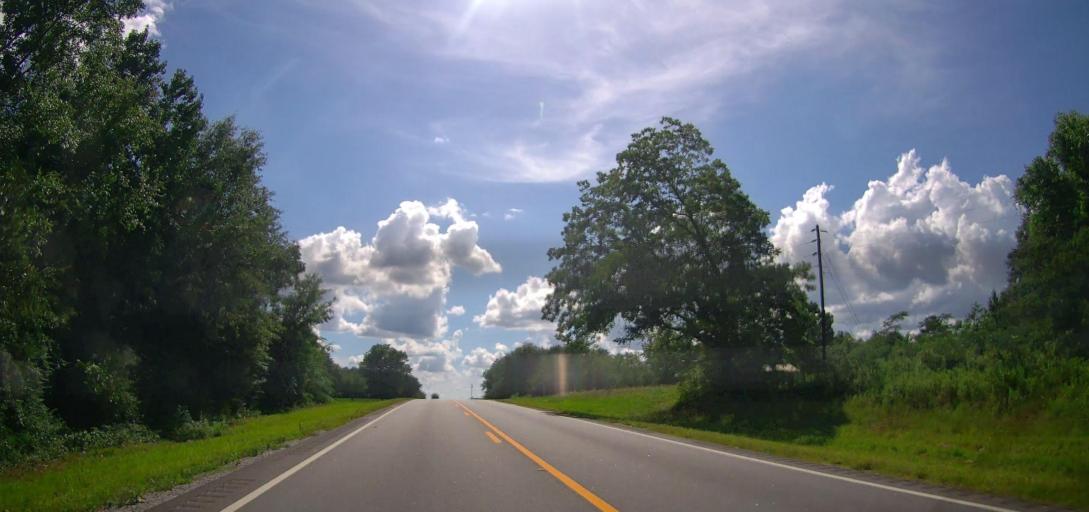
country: US
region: Alabama
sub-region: Lee County
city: Auburn
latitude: 32.4333
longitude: -85.4201
